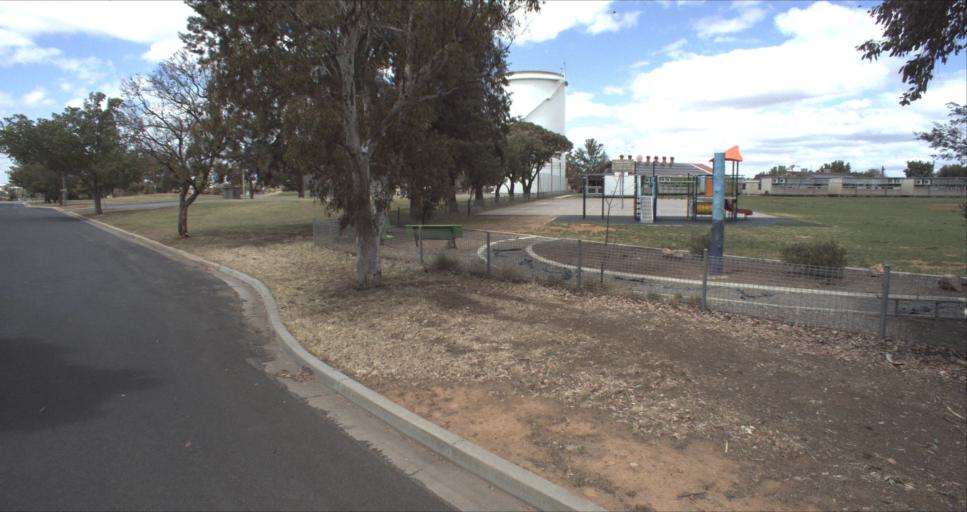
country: AU
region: New South Wales
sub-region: Leeton
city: Leeton
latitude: -34.5609
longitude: 146.3951
